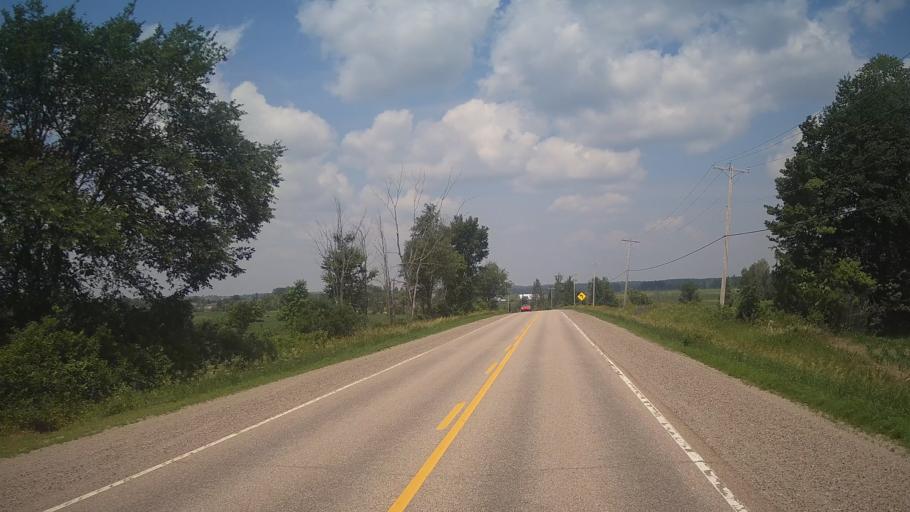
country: CA
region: Quebec
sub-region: Outaouais
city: Shawville
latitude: 45.5809
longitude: -76.4506
